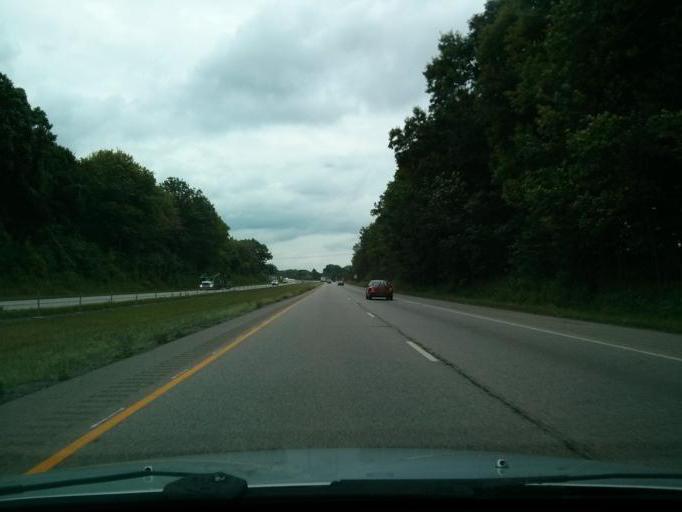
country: US
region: Ohio
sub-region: Portage County
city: Ravenna
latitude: 41.1094
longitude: -81.2289
